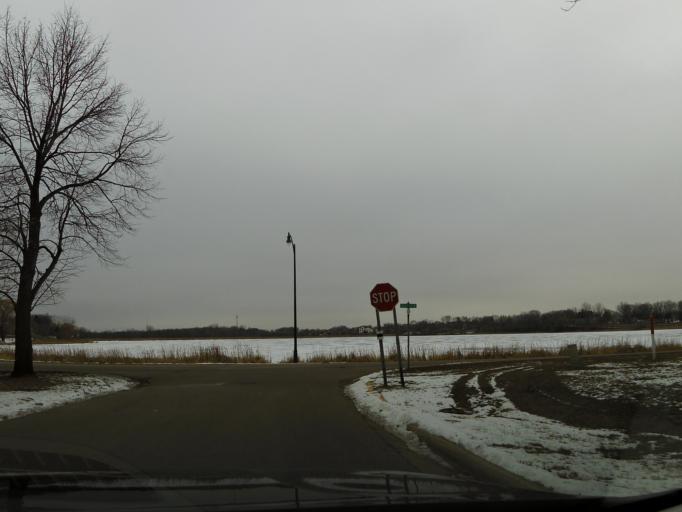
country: US
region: Minnesota
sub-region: Carver County
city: Cologne
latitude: 44.7735
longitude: -93.7806
